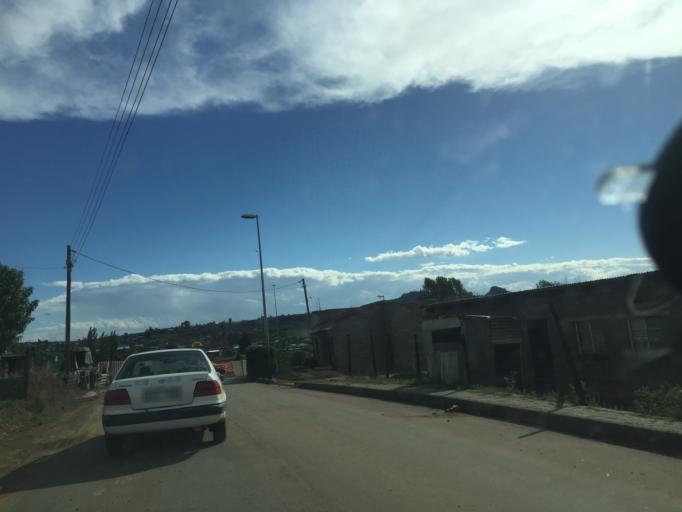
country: LS
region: Maseru
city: Maseru
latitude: -29.3137
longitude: 27.5380
